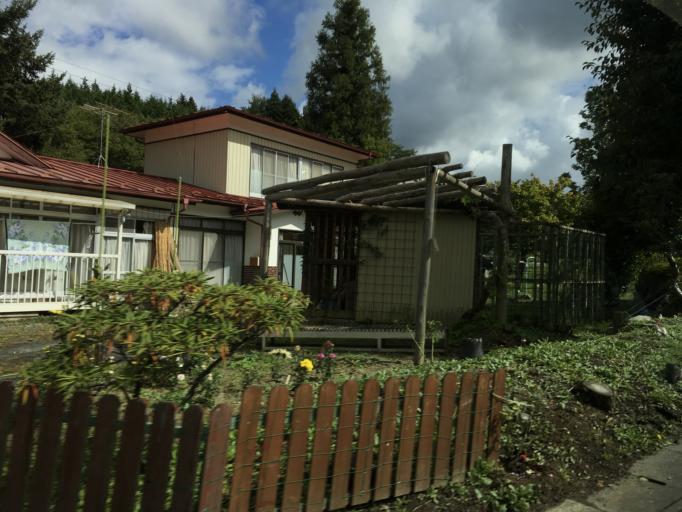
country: JP
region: Iwate
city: Ichinoseki
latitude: 38.8338
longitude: 141.3565
